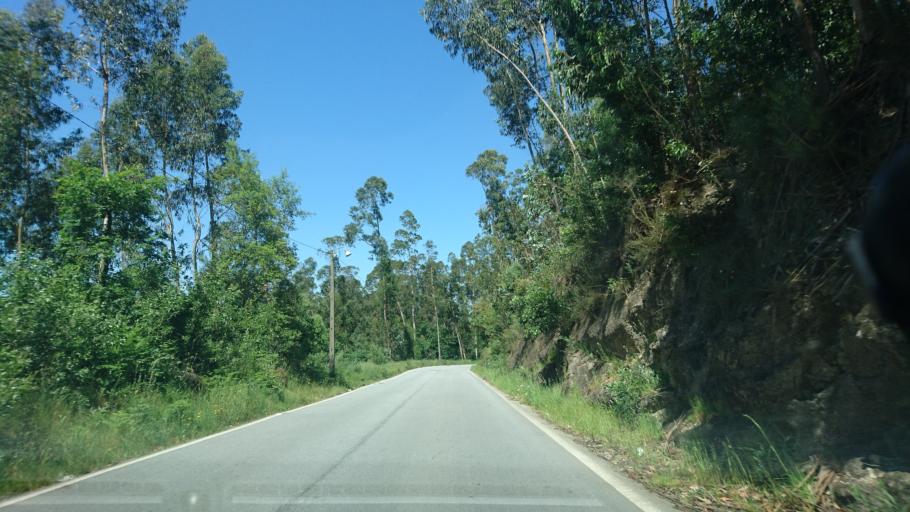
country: PT
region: Porto
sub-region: Paredes
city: Baltar
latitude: 41.1554
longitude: -8.3615
